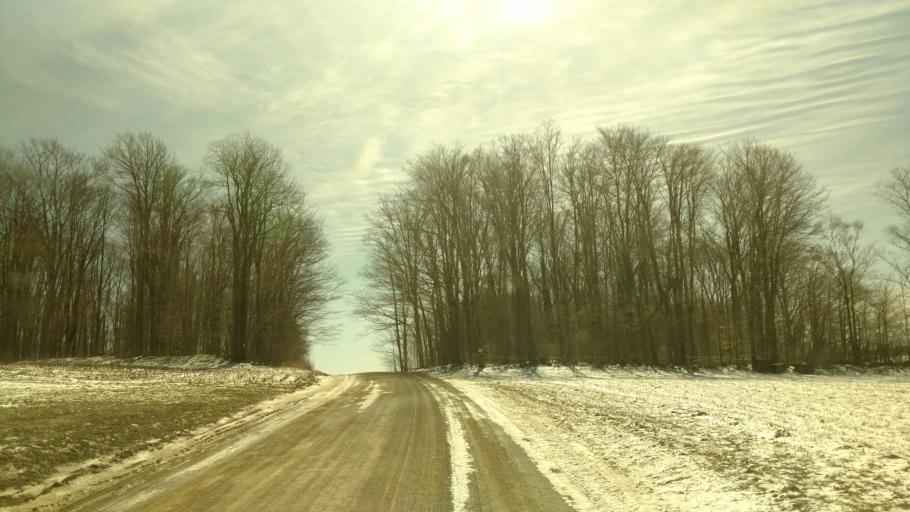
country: US
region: New York
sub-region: Allegany County
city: Andover
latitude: 41.9379
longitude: -77.7693
